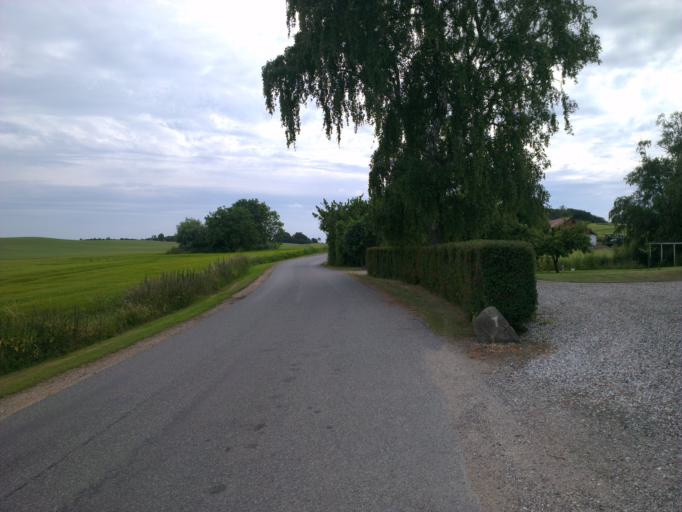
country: DK
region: Capital Region
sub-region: Frederikssund Kommune
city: Skibby
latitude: 55.7522
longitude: 12.0104
